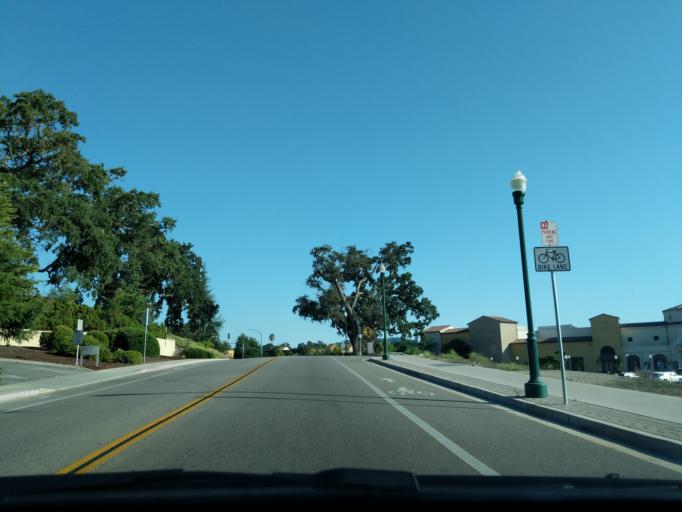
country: US
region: California
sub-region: San Luis Obispo County
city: Atascadero
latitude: 35.4888
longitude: -120.6646
